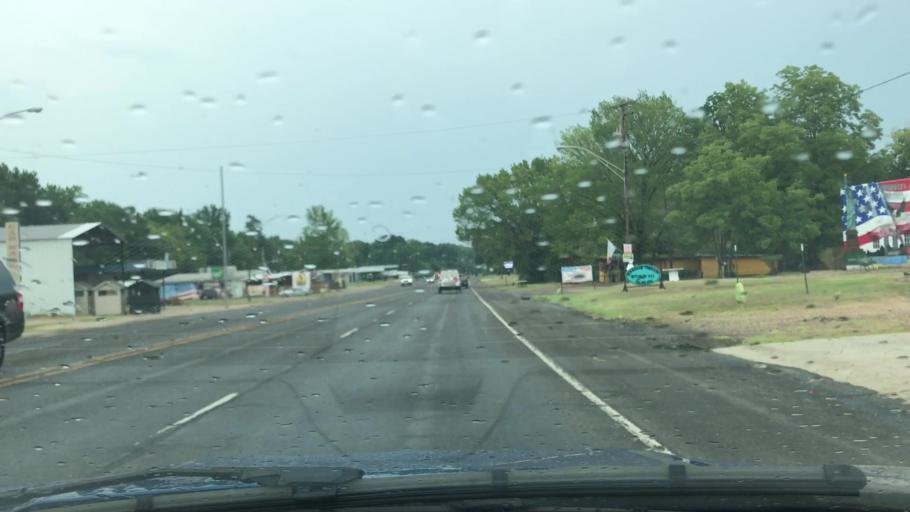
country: US
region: Texas
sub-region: Harrison County
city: Waskom
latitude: 32.4786
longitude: -94.0580
